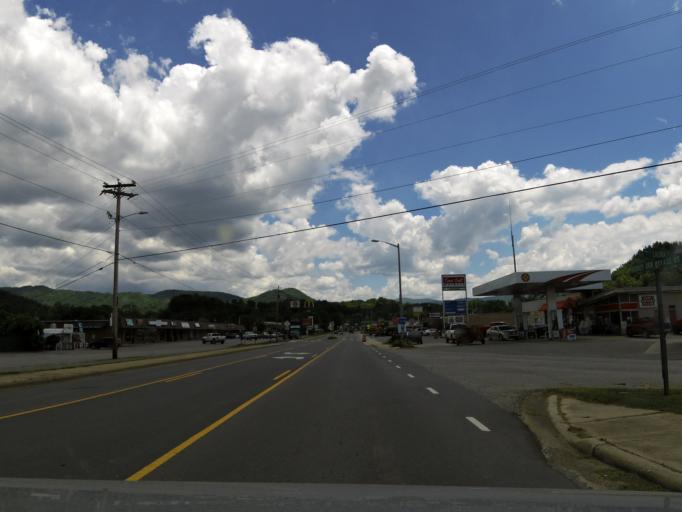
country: US
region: North Carolina
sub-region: Graham County
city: Robbinsville
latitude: 35.3272
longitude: -83.8054
